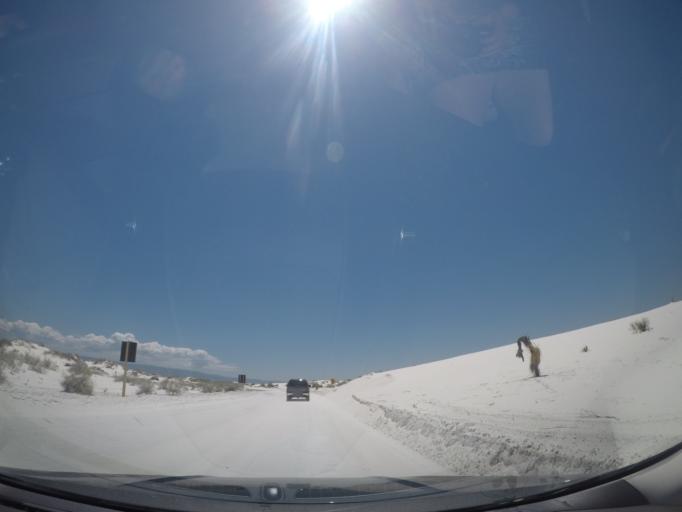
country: US
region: New Mexico
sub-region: Otero County
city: Holloman Air Force Base
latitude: 32.7957
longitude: -106.2454
